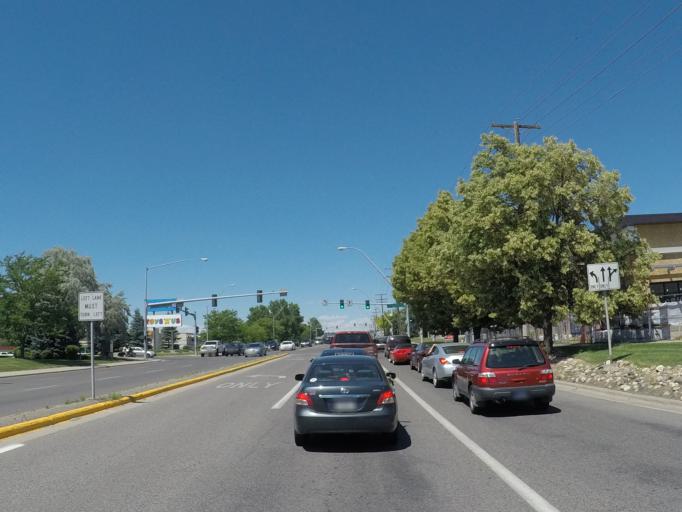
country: US
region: Montana
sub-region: Yellowstone County
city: Billings
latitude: 45.7564
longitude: -108.5761
